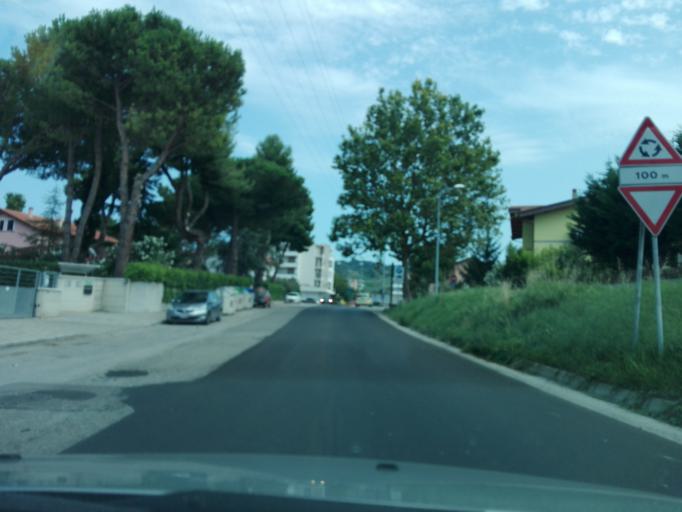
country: IT
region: Abruzzo
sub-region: Provincia di Pescara
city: Montesilvano Marina
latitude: 42.5035
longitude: 14.1339
